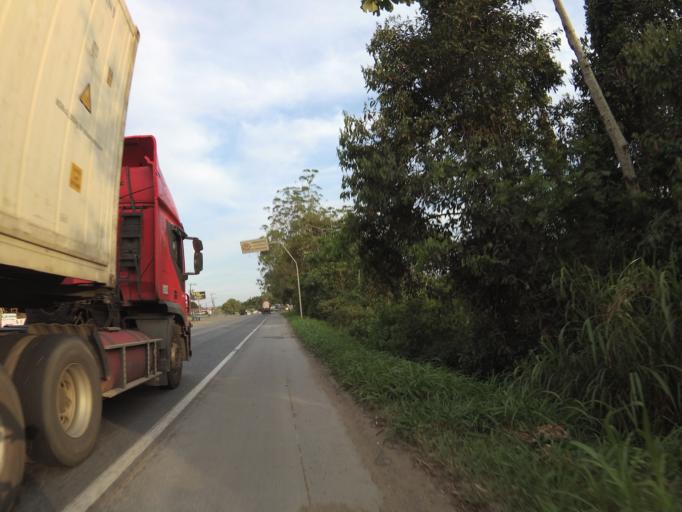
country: BR
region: Santa Catarina
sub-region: Indaial
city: Indaial
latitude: -26.8785
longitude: -49.1752
